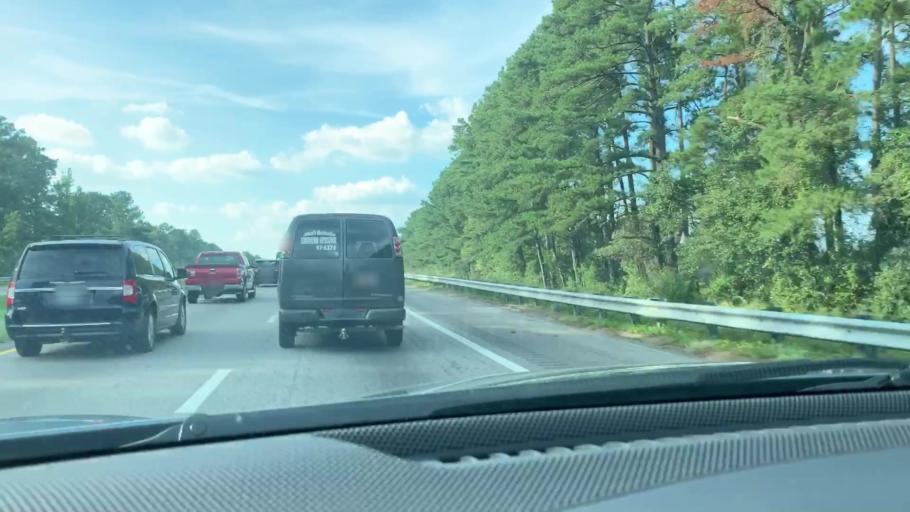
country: US
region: South Carolina
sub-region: Orangeburg County
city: Brookdale
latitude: 33.5169
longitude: -80.7879
